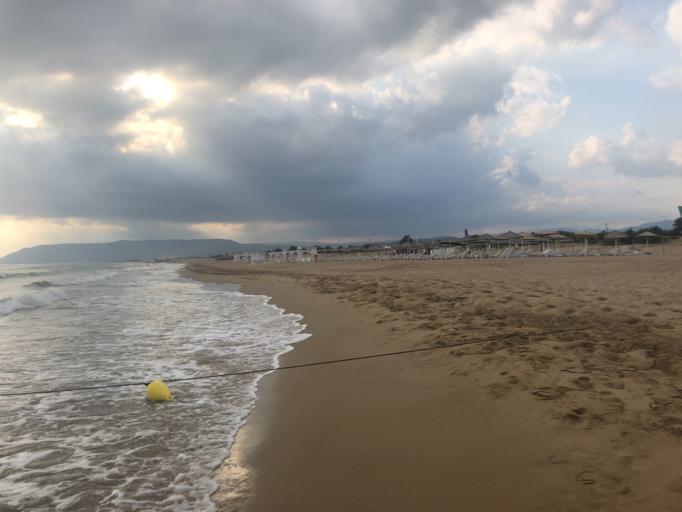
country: GR
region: Crete
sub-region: Nomos Chanias
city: Georgioupolis
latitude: 35.3564
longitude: 24.2806
